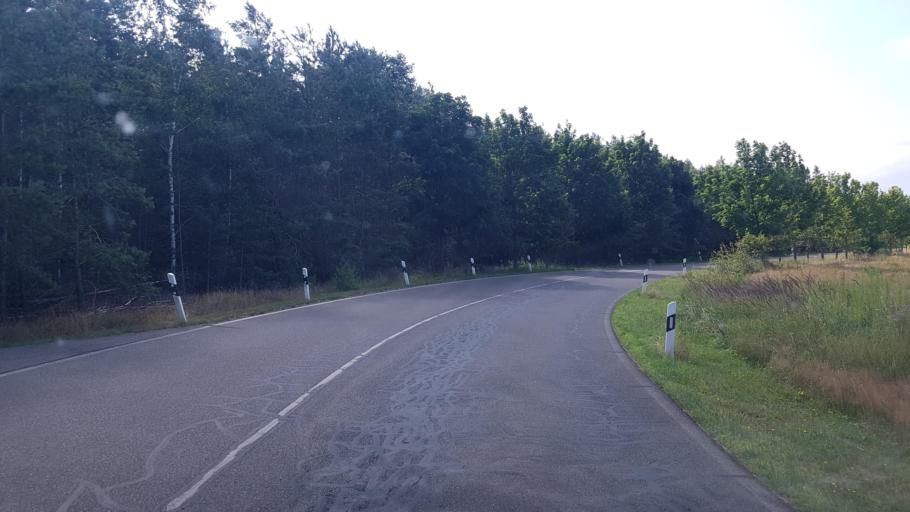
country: DE
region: Brandenburg
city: Grossraschen
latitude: 51.5936
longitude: 14.0282
